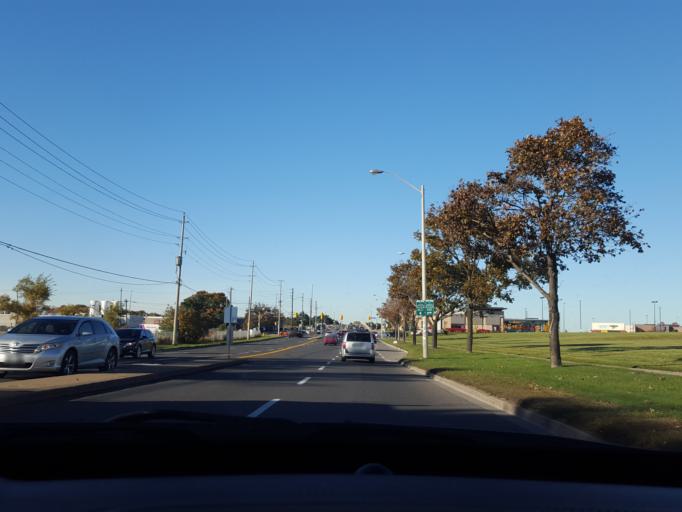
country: CA
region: Ontario
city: Scarborough
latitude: 43.7736
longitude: -79.2624
